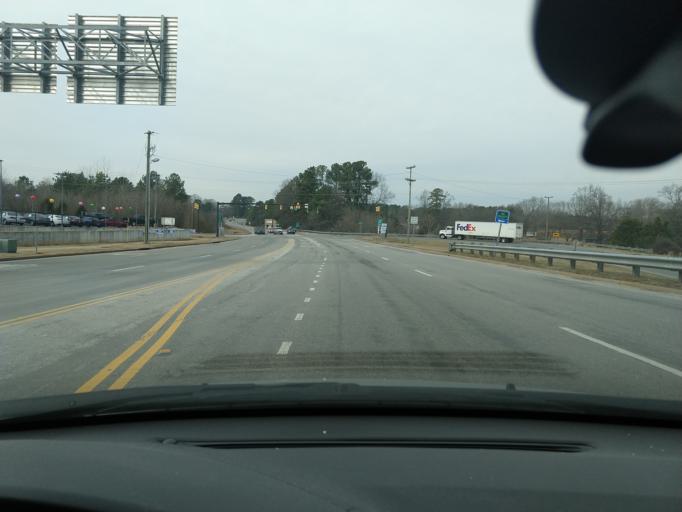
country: US
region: South Carolina
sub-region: Cherokee County
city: Gaffney
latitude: 35.0990
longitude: -81.6706
